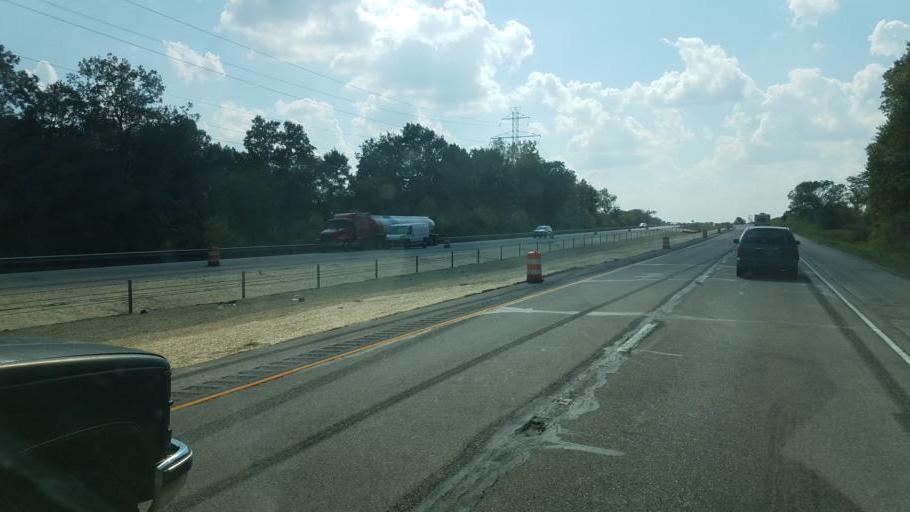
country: US
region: Indiana
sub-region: Allen County
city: Huntertown
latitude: 41.2296
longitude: -85.0991
